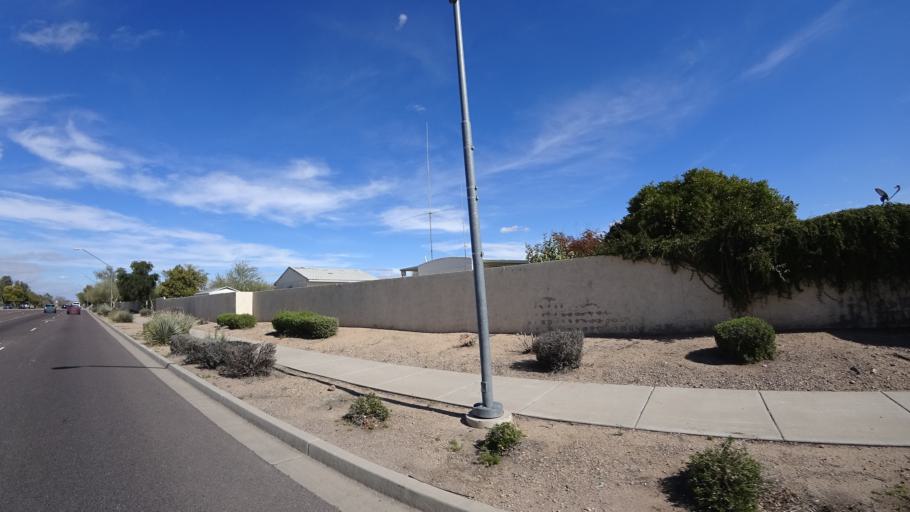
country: US
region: Arizona
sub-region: Maricopa County
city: Peoria
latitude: 33.6423
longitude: -112.2029
